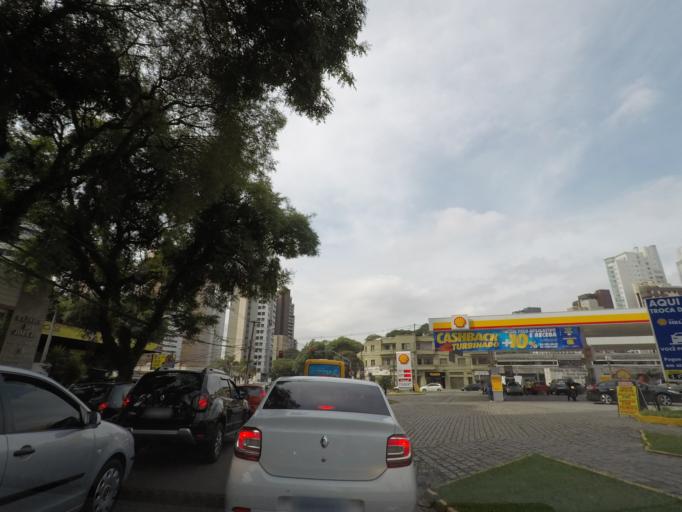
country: BR
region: Parana
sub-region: Curitiba
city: Curitiba
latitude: -25.4514
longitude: -49.2887
